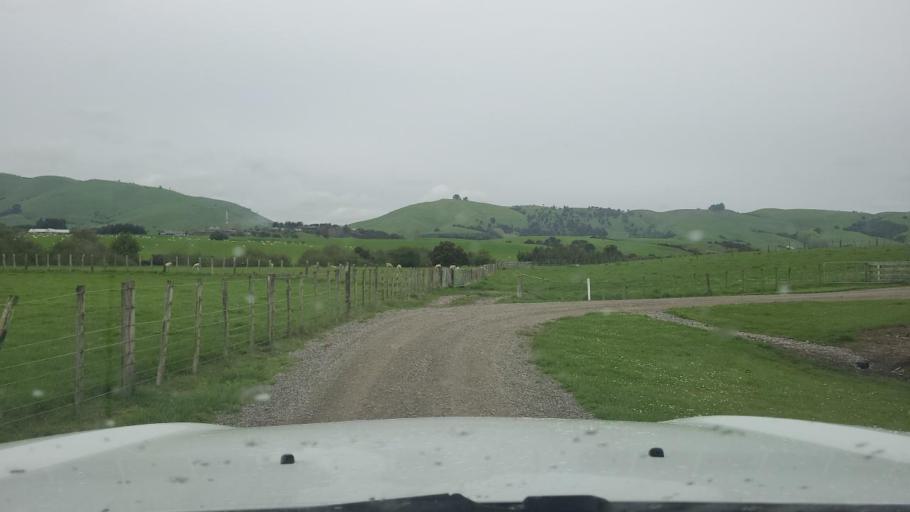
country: NZ
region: Wellington
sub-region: Masterton District
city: Masterton
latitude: -41.0740
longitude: 175.6634
